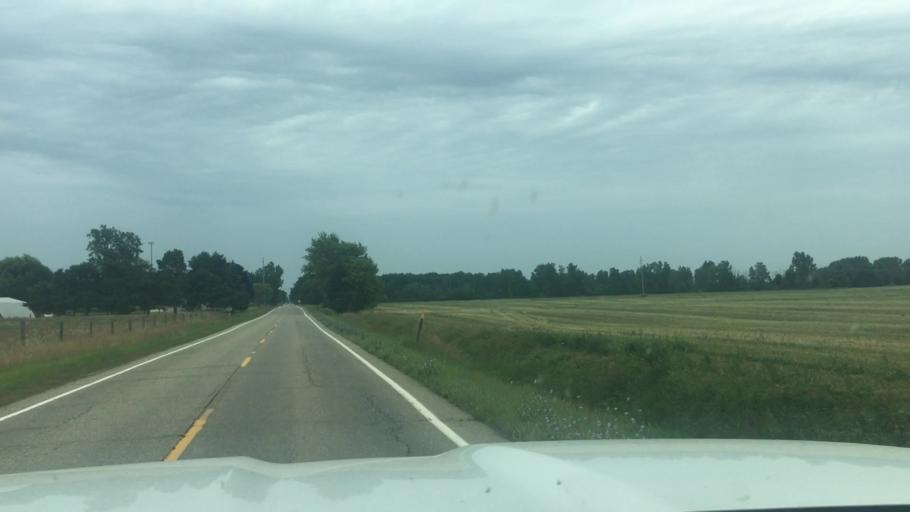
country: US
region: Michigan
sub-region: Clinton County
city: Saint Johns
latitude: 43.0115
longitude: -84.4841
